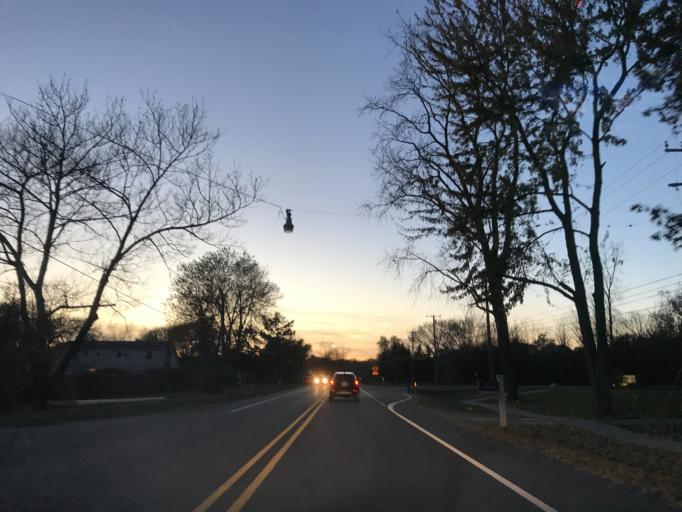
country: US
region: Michigan
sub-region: Oakland County
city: Farmington
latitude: 42.4698
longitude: -83.3720
